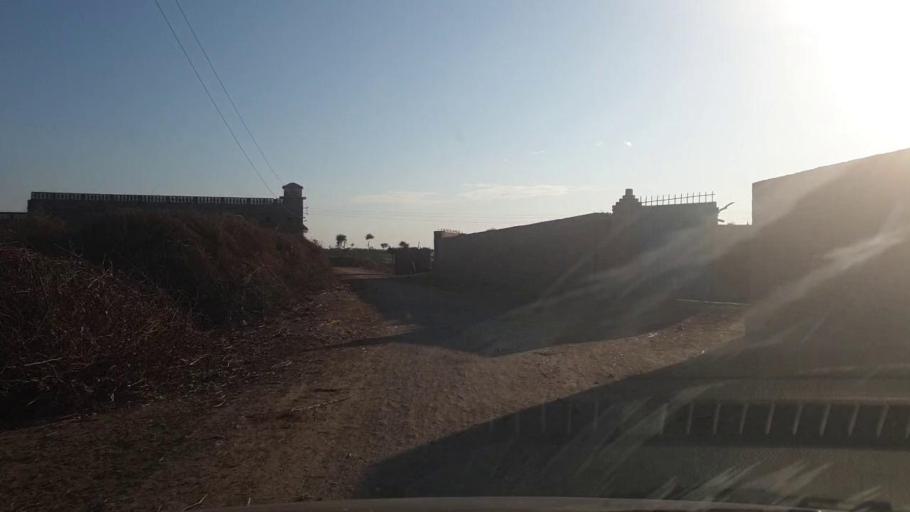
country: PK
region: Sindh
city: Sinjhoro
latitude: 26.0461
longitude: 68.8691
